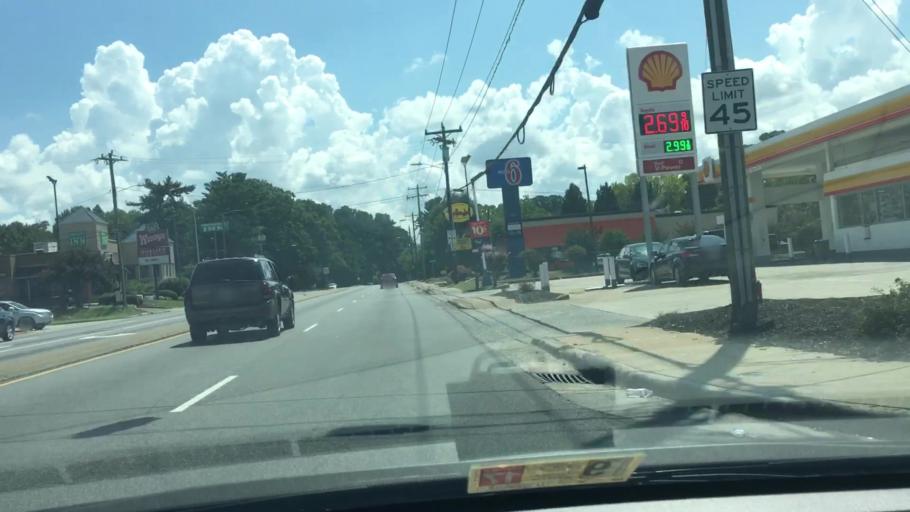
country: US
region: North Carolina
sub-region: Mecklenburg County
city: Charlotte
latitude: 35.2764
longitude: -80.7936
